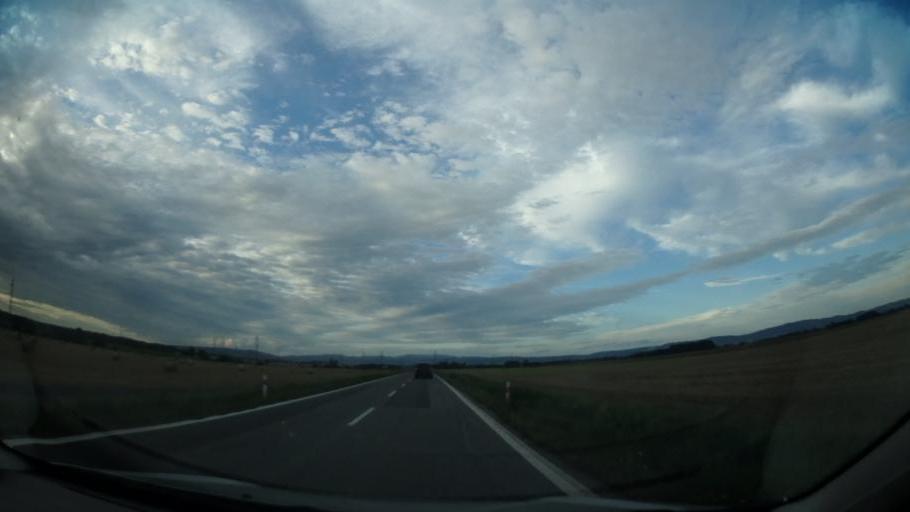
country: CZ
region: Olomoucky
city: Cervenka
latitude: 49.7299
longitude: 17.0831
